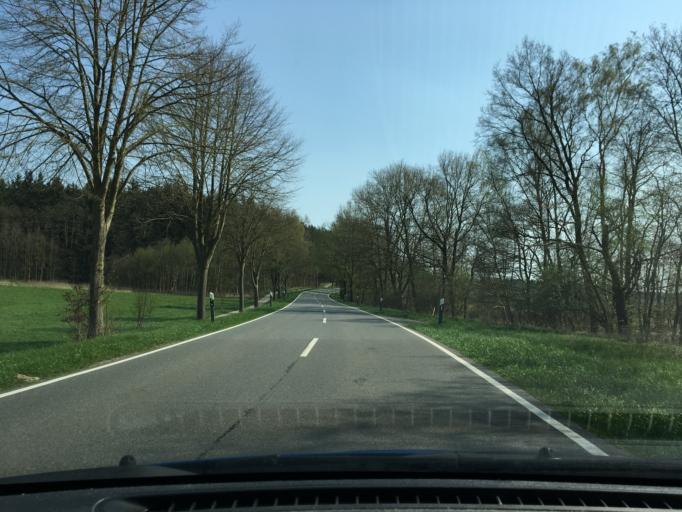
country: DE
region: Lower Saxony
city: Sudergellersen
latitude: 53.1979
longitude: 10.3052
